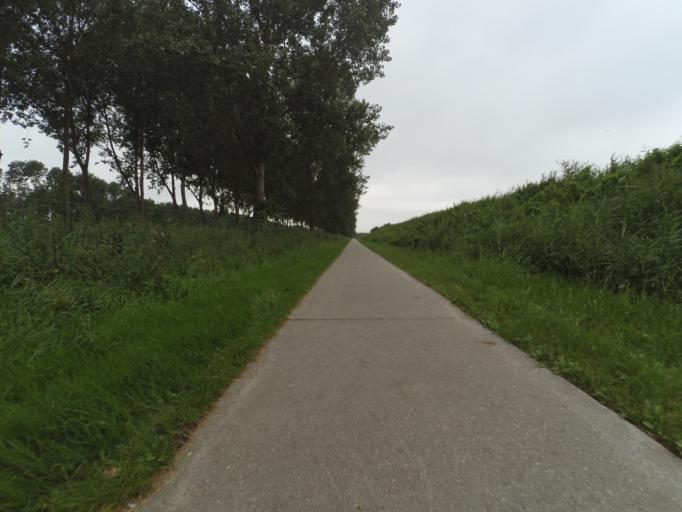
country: NL
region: Flevoland
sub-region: Gemeente Almere
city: Almere Stad
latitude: 52.4120
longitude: 5.3116
